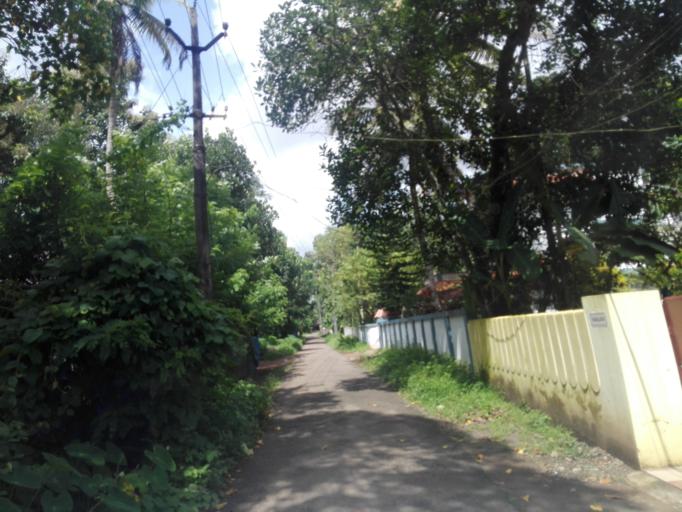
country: IN
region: Kerala
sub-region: Alappuzha
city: Arukutti
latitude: 9.8301
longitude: 76.3895
